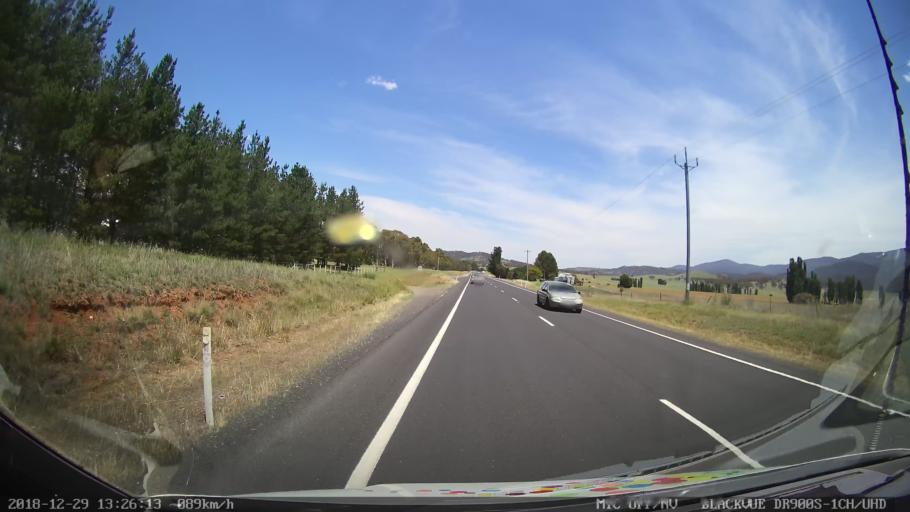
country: AU
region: New South Wales
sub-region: Cooma-Monaro
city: Cooma
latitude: -35.8527
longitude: 149.1595
